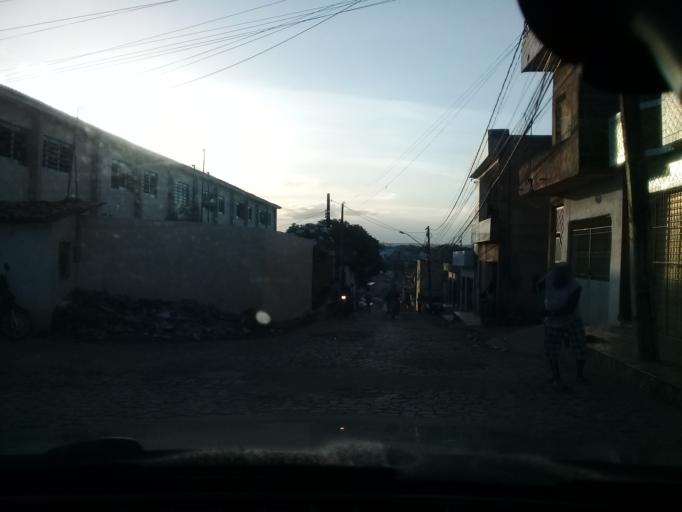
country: BR
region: Pernambuco
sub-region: Vitoria De Santo Antao
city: Vitoria de Santo Antao
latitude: -8.1297
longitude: -35.2937
